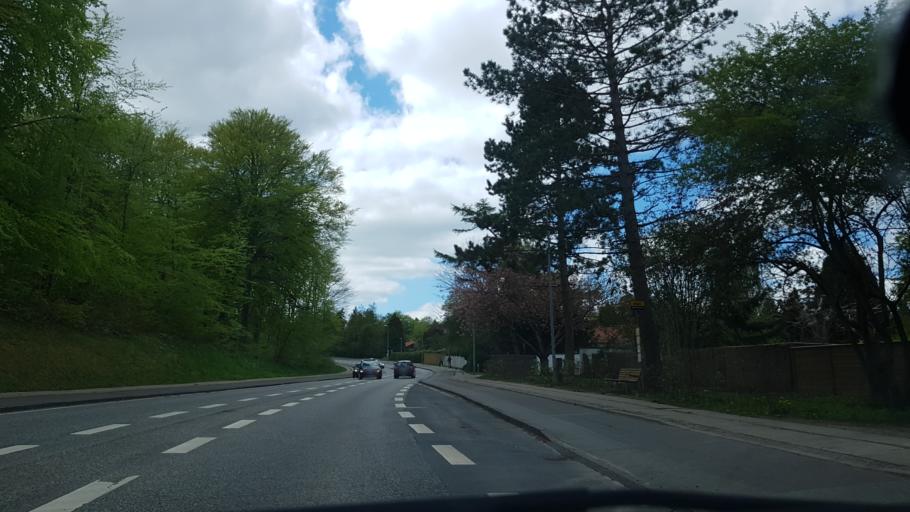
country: DK
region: Capital Region
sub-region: Horsholm Kommune
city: Horsholm
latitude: 55.8826
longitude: 12.5216
